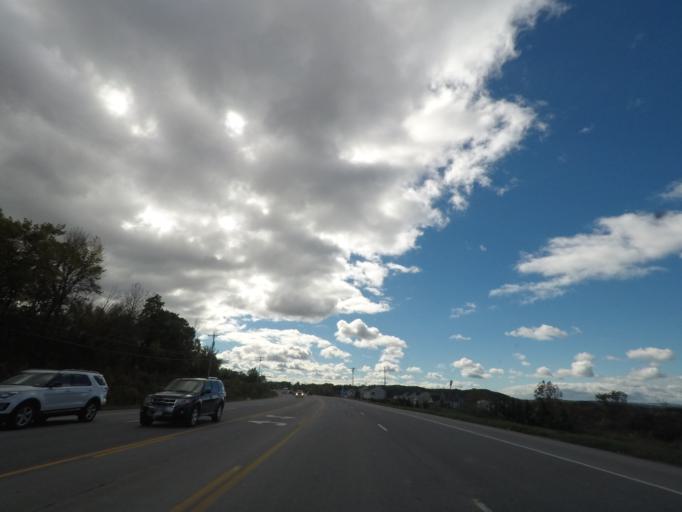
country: US
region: New York
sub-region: Albany County
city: Cohoes
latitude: 42.8071
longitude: -73.7338
